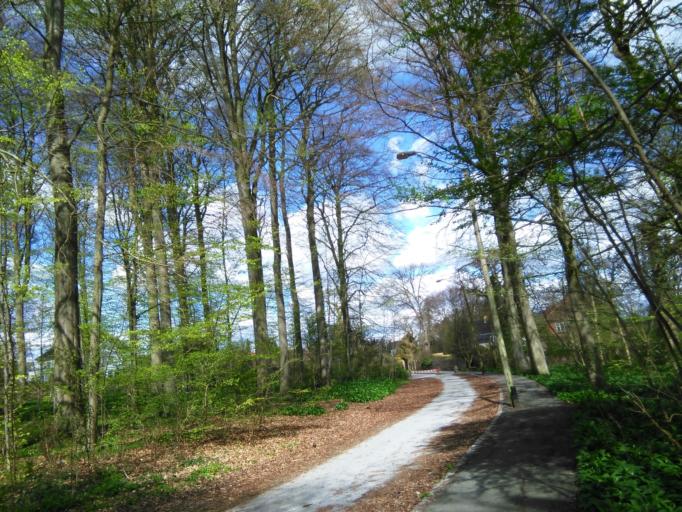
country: DK
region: Central Jutland
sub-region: Arhus Kommune
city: Arhus
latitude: 56.1812
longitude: 10.2298
